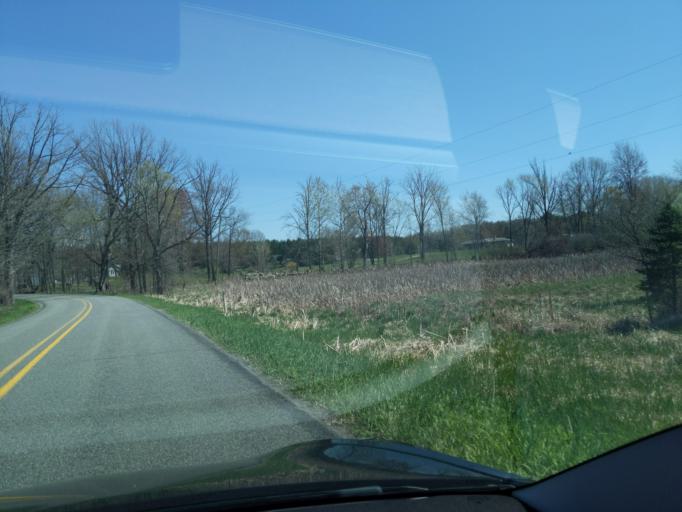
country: US
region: Michigan
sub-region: Ingham County
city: Stockbridge
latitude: 42.4870
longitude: -84.1811
